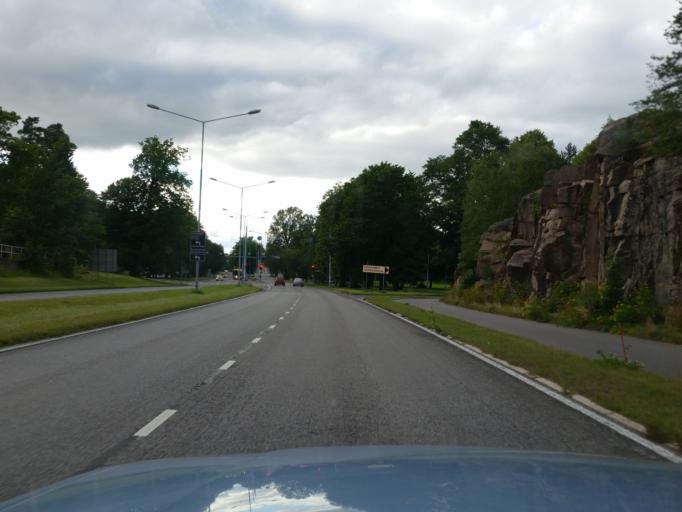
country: FI
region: Varsinais-Suomi
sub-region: Turku
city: Turku
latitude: 60.4344
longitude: 22.2976
